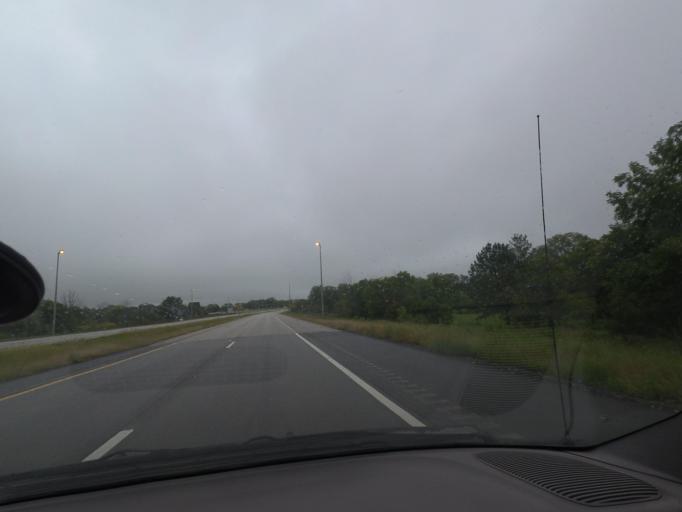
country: US
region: Illinois
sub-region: Macon County
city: Harristown
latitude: 39.8431
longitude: -89.0383
